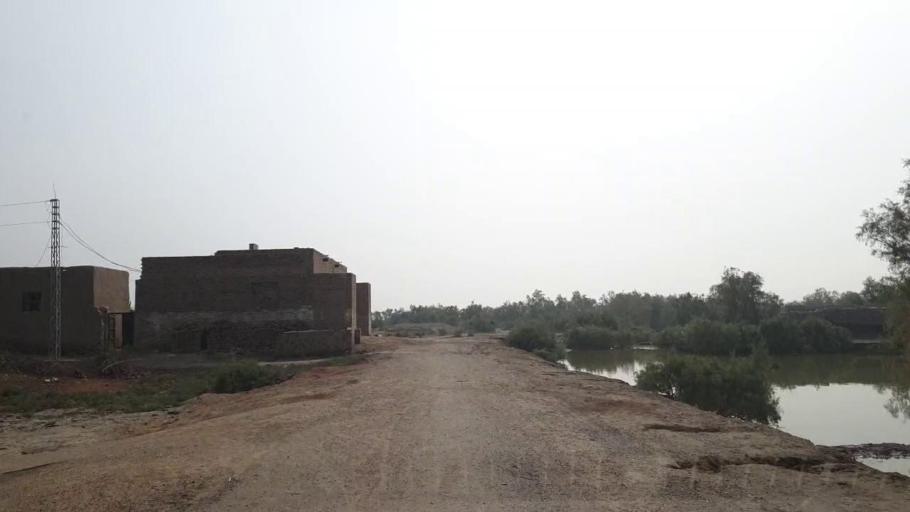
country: PK
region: Sindh
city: Bhan
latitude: 26.5084
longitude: 67.6734
